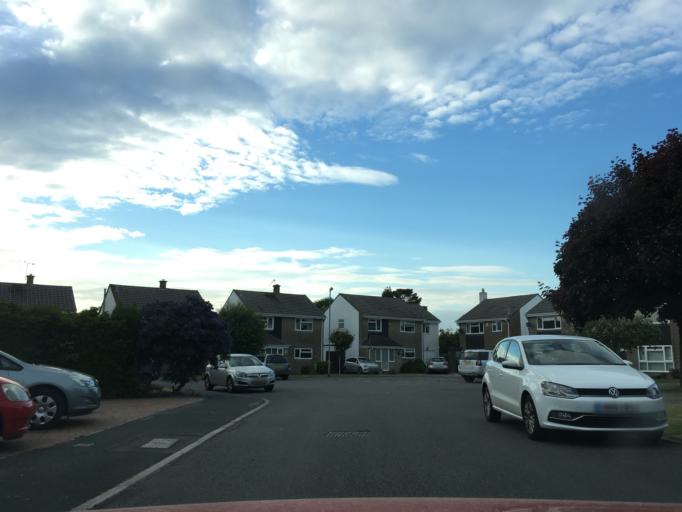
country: GB
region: England
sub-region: South Gloucestershire
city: Almondsbury
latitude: 51.5569
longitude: -2.5614
